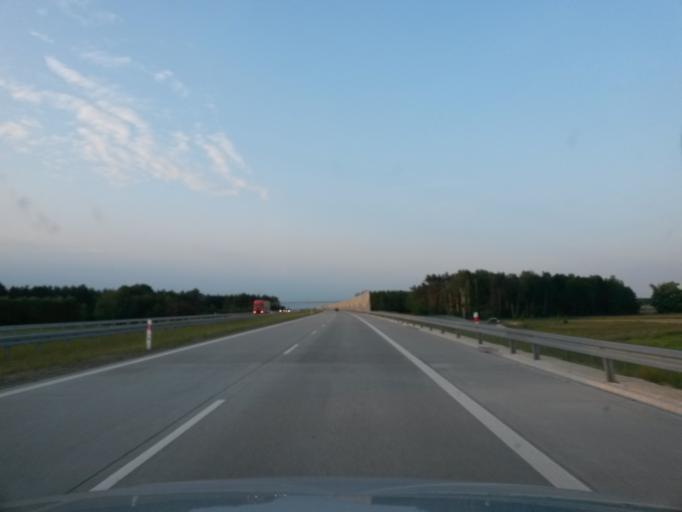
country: PL
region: Lodz Voivodeship
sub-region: Powiat wieruszowski
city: Lututow
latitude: 51.3423
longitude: 18.4998
